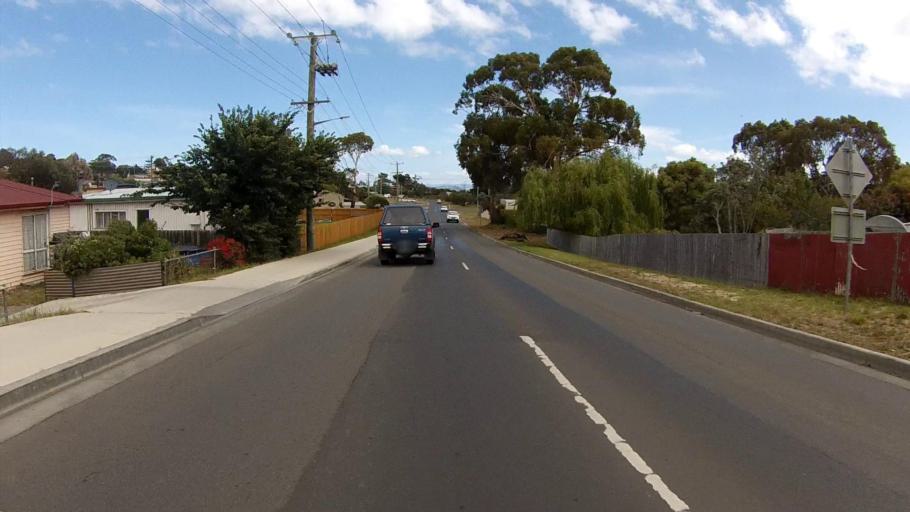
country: AU
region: Tasmania
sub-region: Sorell
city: Sorell
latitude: -42.8580
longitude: 147.6163
